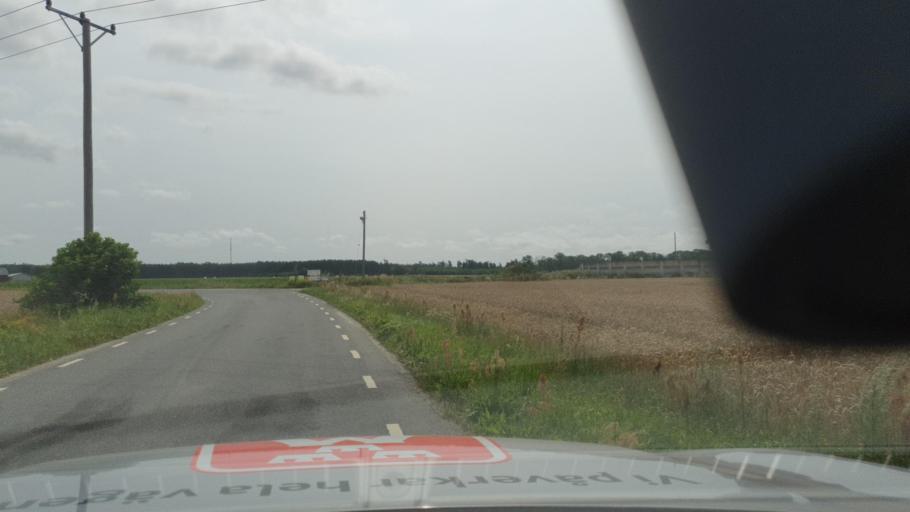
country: SE
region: Skane
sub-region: Bromolla Kommun
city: Bromoella
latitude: 56.0470
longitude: 14.3946
